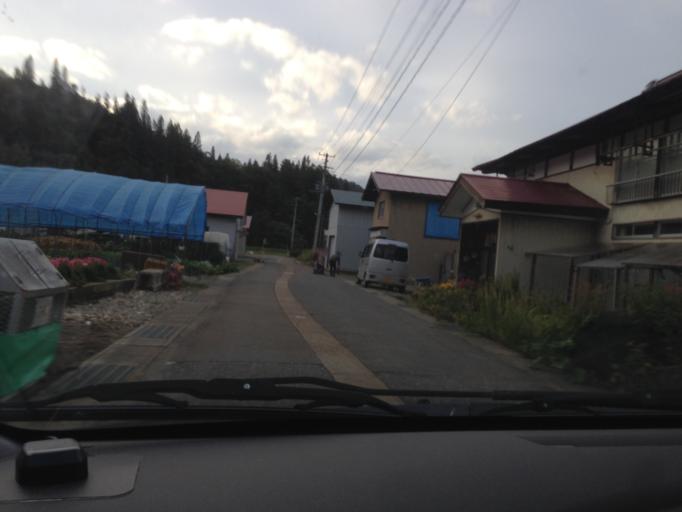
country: JP
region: Fukushima
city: Kitakata
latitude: 37.3565
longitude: 139.5770
